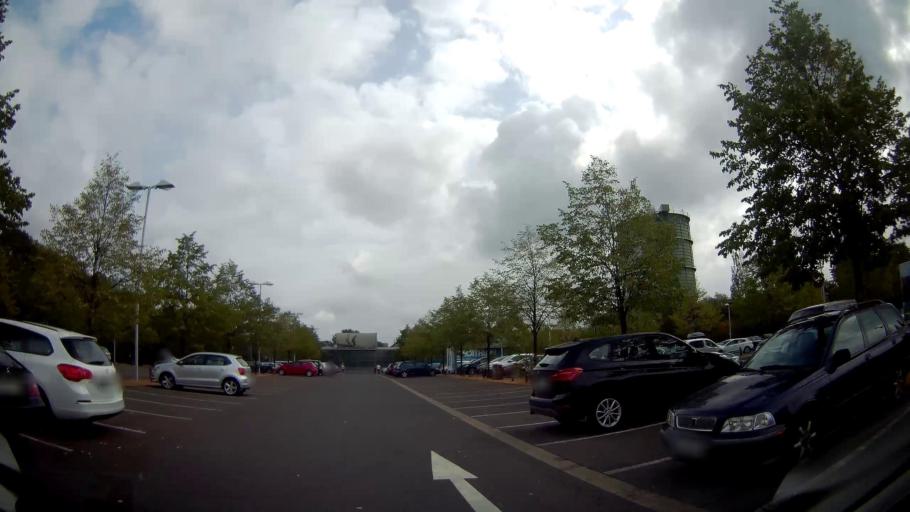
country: DE
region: North Rhine-Westphalia
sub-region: Regierungsbezirk Arnsberg
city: Herne
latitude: 51.5295
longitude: 7.2017
